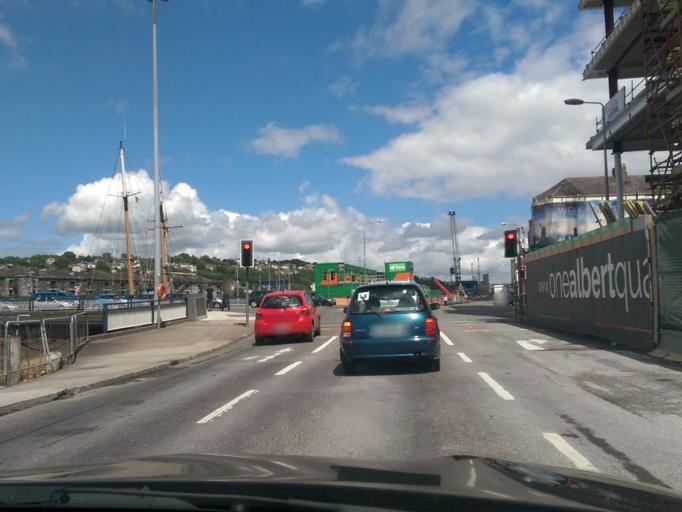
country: IE
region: Munster
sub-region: County Cork
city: Cork
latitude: 51.8979
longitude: -8.4640
